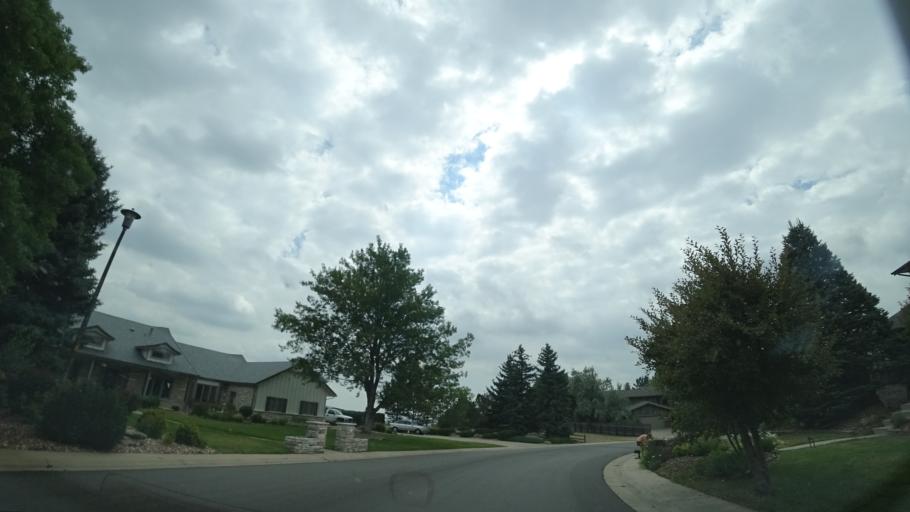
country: US
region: Colorado
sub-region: Jefferson County
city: West Pleasant View
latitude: 39.7130
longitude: -105.1651
